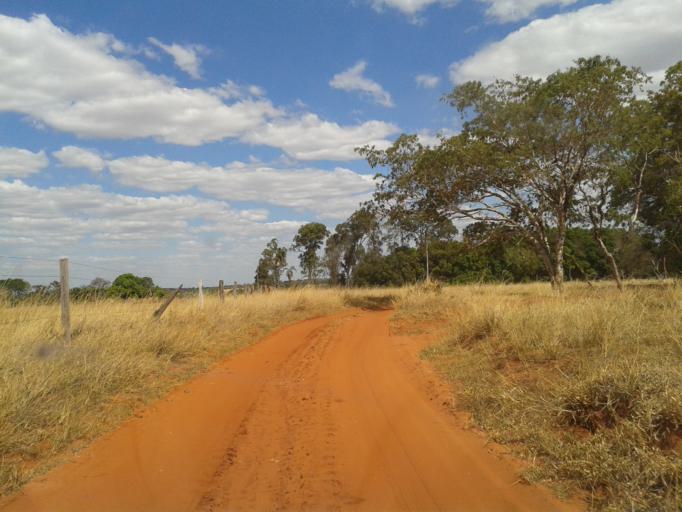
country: BR
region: Minas Gerais
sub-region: Centralina
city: Centralina
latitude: -18.7753
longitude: -49.0897
